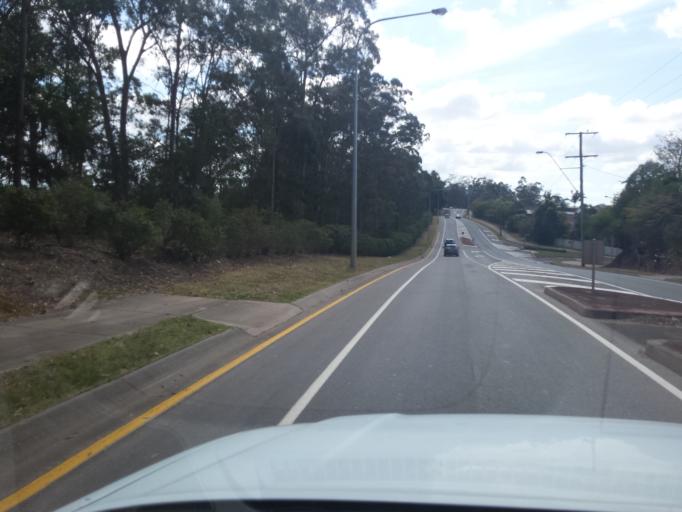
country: AU
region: Queensland
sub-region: Moreton Bay
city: Ferny Hills
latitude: -27.3820
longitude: 152.9442
